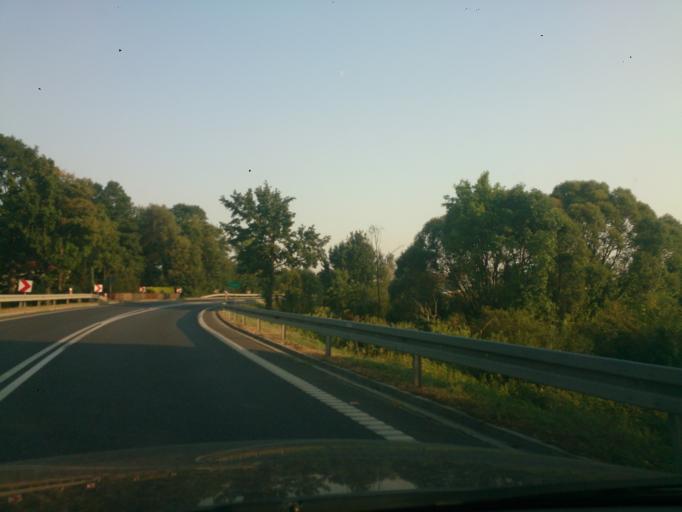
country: PL
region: Subcarpathian Voivodeship
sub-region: Powiat kolbuszowski
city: Cmolas
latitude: 50.2754
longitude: 21.7578
